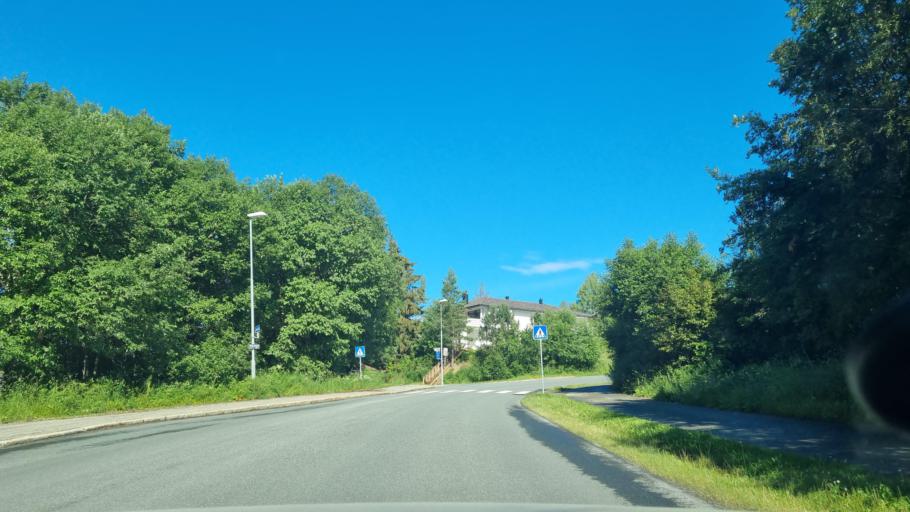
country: NO
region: Sor-Trondelag
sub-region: Trondheim
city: Trondheim
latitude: 63.3834
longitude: 10.3281
